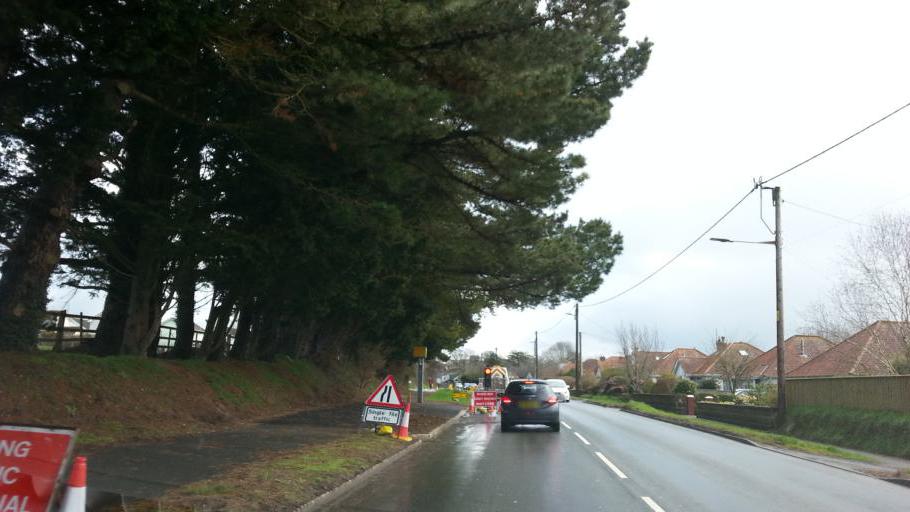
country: GB
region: England
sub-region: Devon
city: Fremington
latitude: 51.0729
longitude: -4.1048
